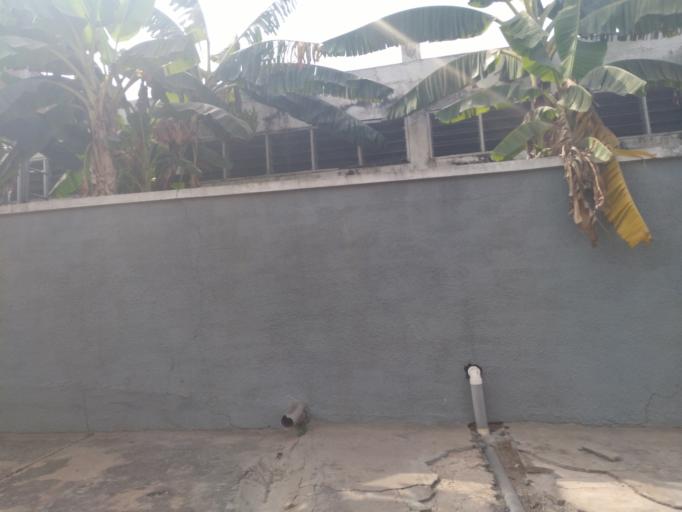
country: GH
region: Ashanti
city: Kumasi
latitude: 6.6842
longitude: -1.6033
